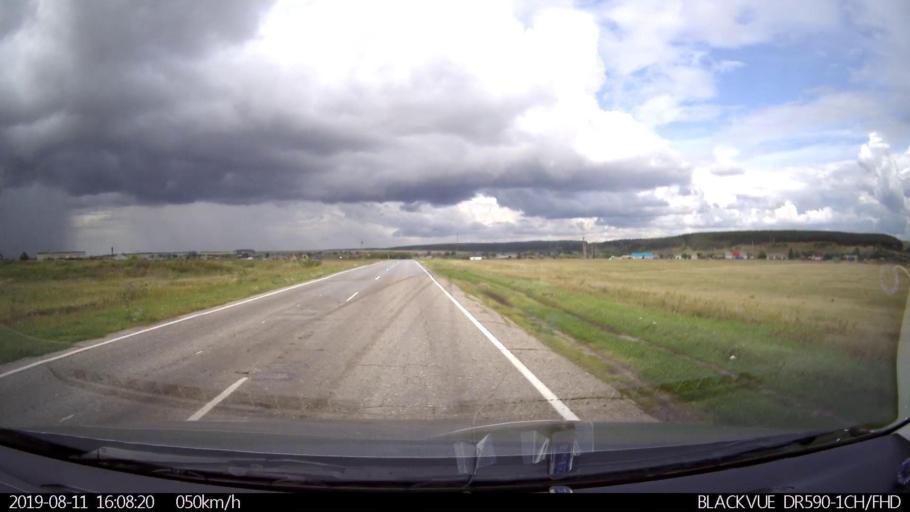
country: RU
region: Ulyanovsk
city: Ignatovka
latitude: 53.9837
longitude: 47.6480
